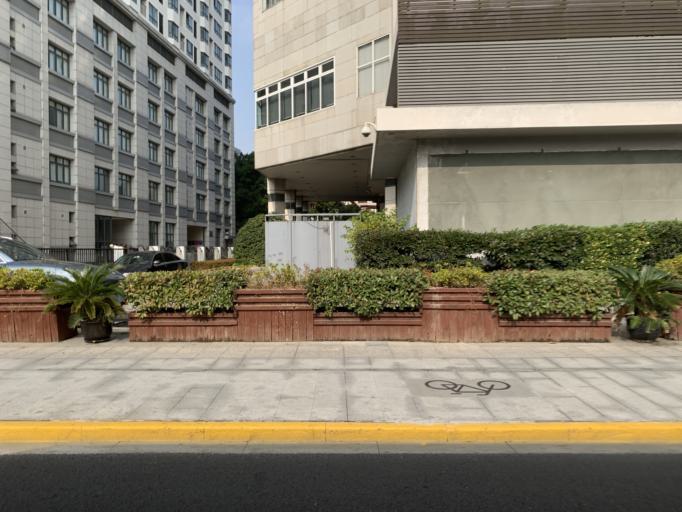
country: CN
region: Shanghai Shi
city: Xuhui
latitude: 31.2031
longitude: 121.4496
